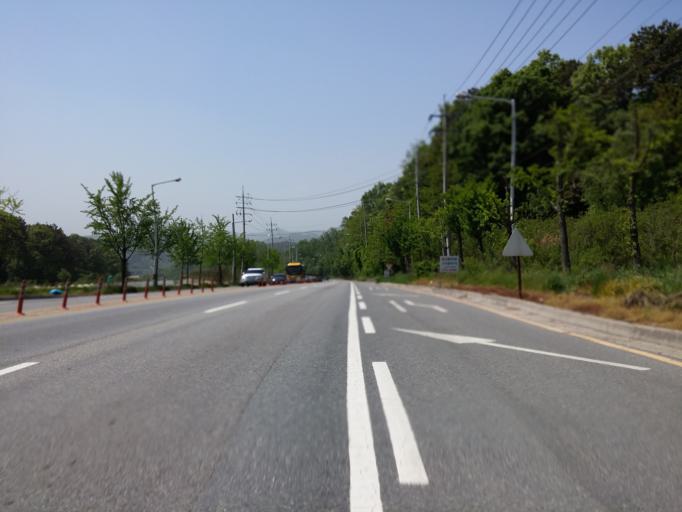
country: KR
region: Daejeon
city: Daejeon
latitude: 36.2759
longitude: 127.2930
